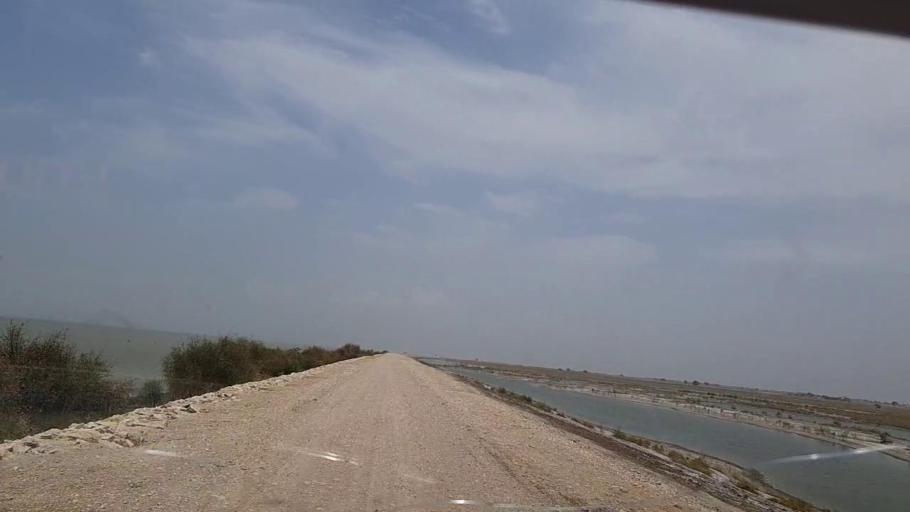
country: PK
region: Sindh
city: Sehwan
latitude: 26.4190
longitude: 67.7366
